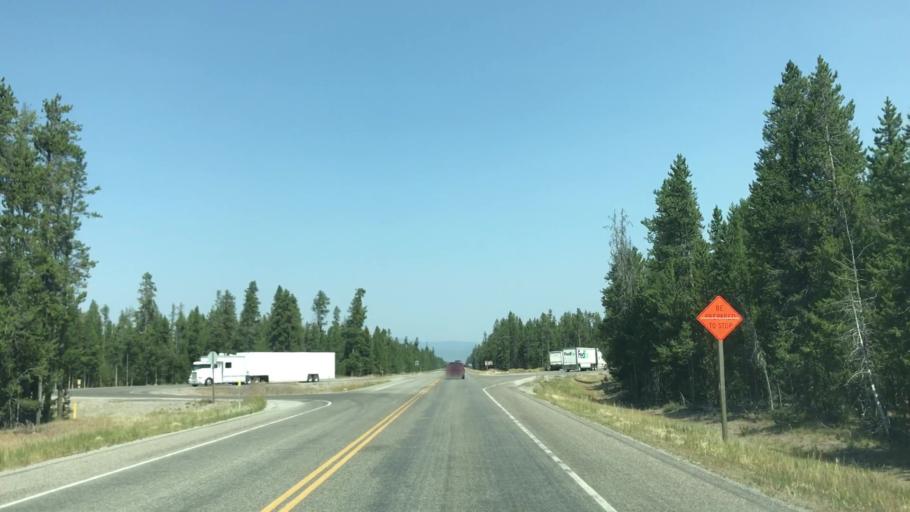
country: US
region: Montana
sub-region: Gallatin County
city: West Yellowstone
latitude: 44.6728
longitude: -111.1003
